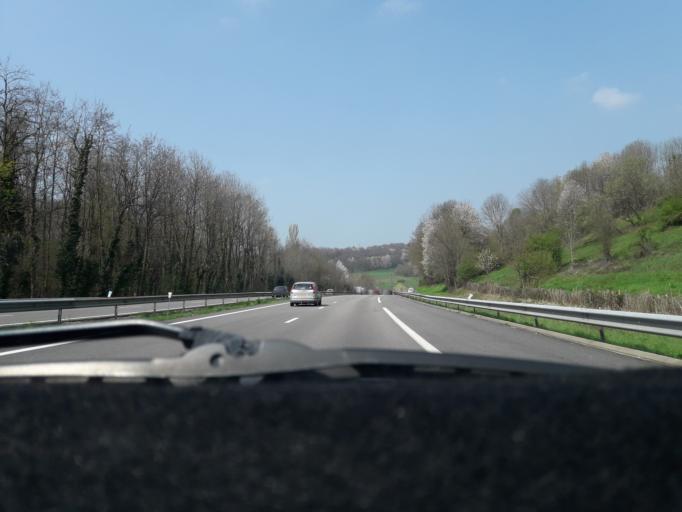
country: FR
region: Rhone-Alpes
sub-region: Departement de l'Isere
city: Charnecles
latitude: 45.3553
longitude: 5.5251
